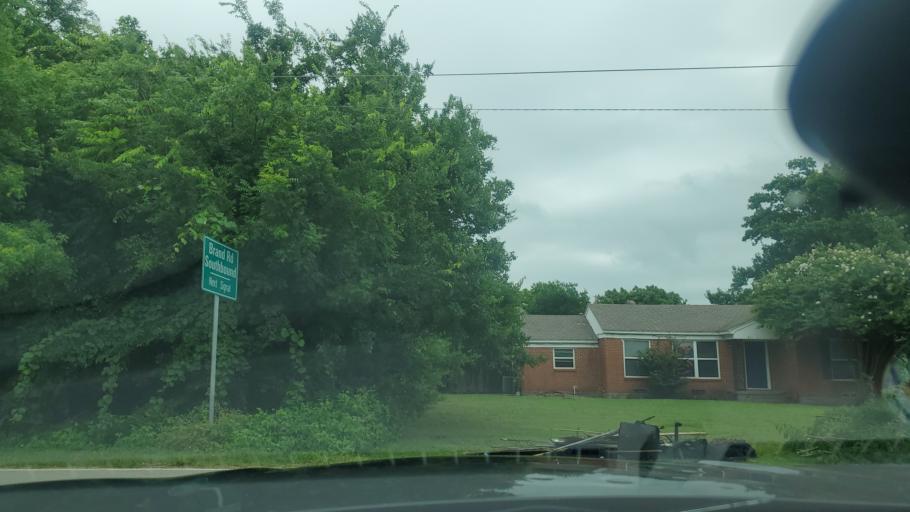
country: US
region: Texas
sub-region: Dallas County
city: Sachse
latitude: 32.9522
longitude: -96.6260
